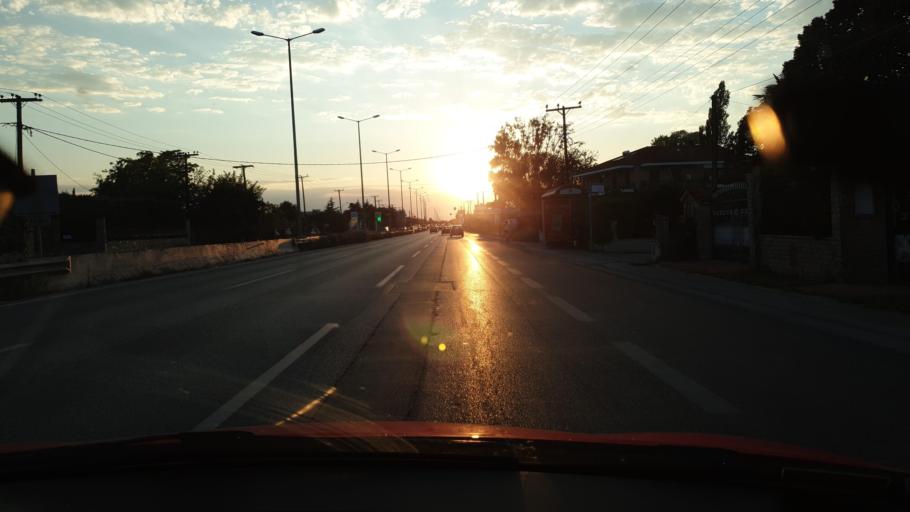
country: GR
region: Central Macedonia
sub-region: Nomos Thessalonikis
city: Plagiari
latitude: 40.5004
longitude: 22.9554
